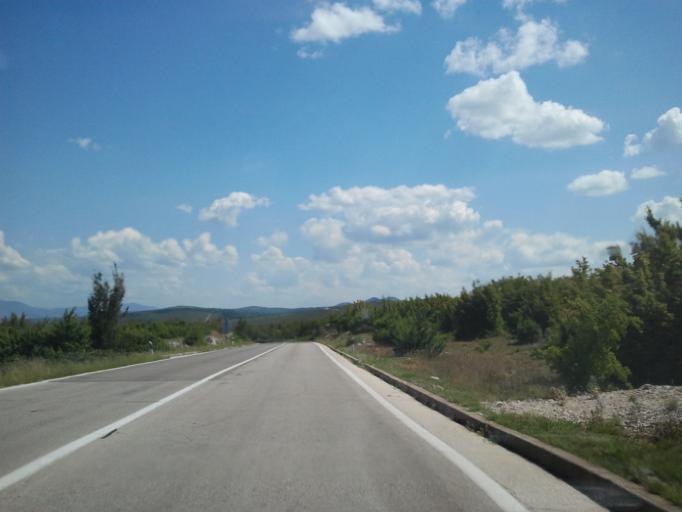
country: HR
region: Zadarska
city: Obrovac
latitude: 44.1965
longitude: 15.6679
